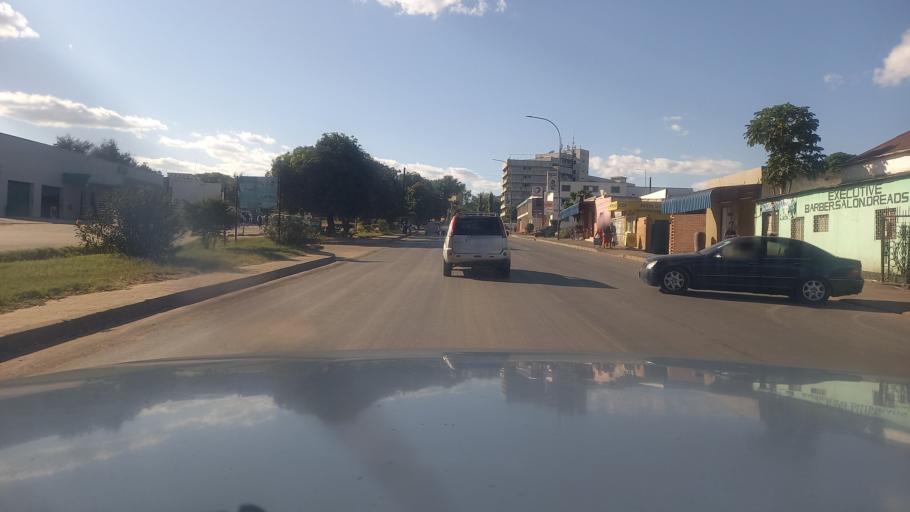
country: ZM
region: Southern
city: Livingstone
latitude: -17.8515
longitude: 25.8552
